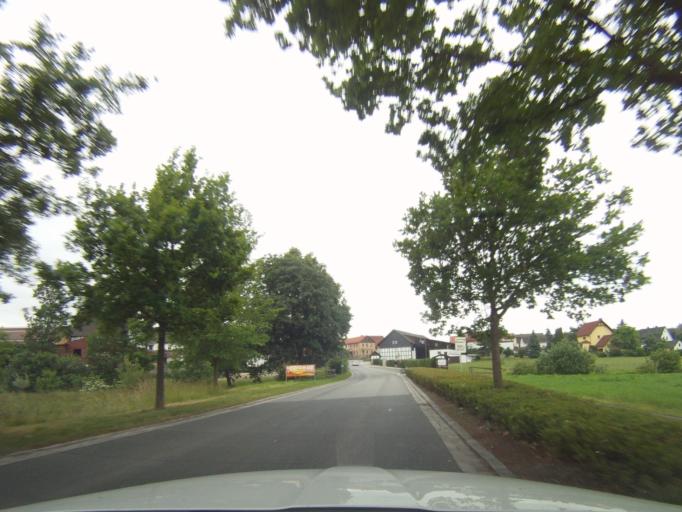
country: DE
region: Bavaria
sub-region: Upper Franconia
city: Ahorn
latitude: 50.2280
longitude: 10.9176
